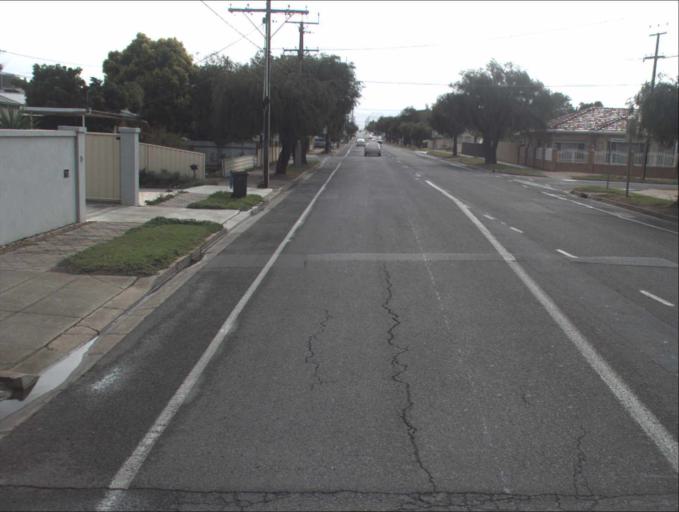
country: AU
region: South Australia
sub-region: Port Adelaide Enfield
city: Klemzig
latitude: -34.8688
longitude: 138.6370
